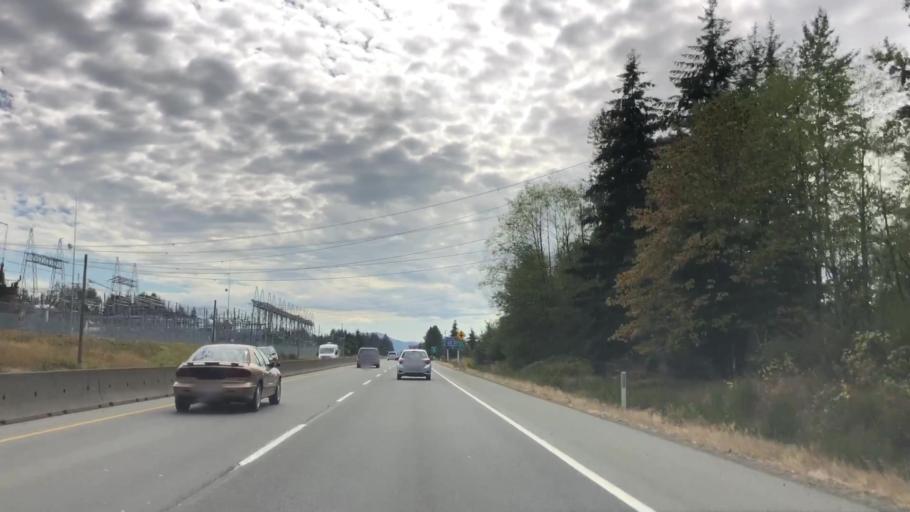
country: CA
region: British Columbia
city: North Cowichan
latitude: 48.8285
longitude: -123.7181
